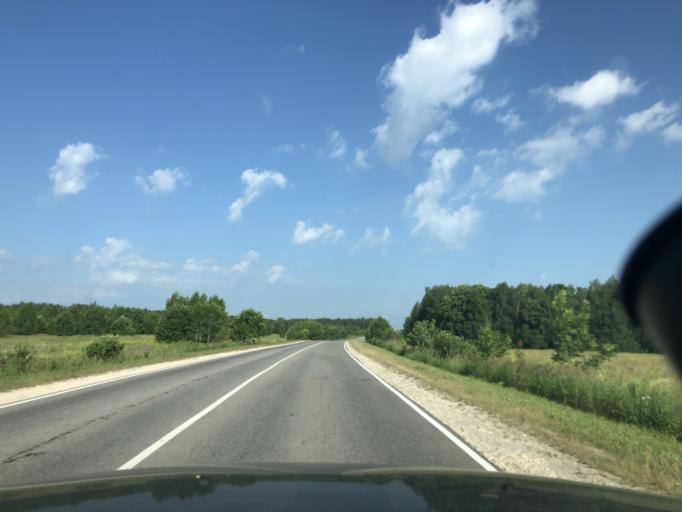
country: RU
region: Tula
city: Dubna
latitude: 54.1327
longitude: 37.0289
